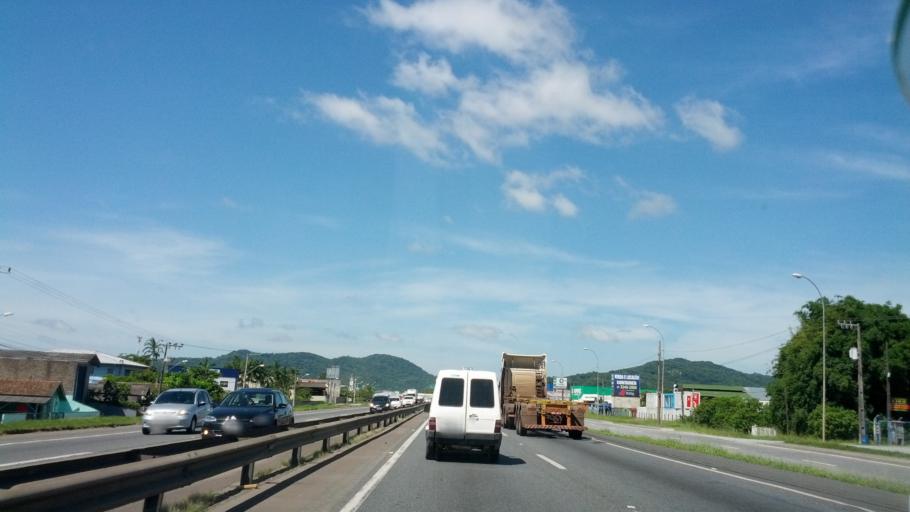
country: BR
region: Santa Catarina
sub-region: Itajai
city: Itajai
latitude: -26.8625
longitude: -48.7288
